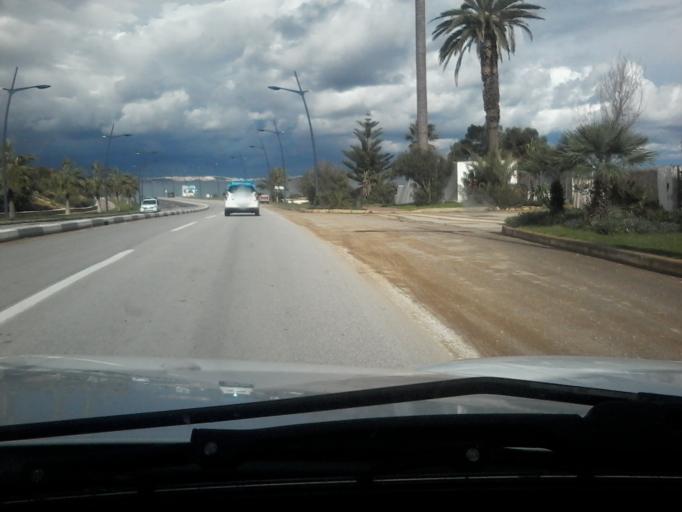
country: ES
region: Ceuta
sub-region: Ceuta
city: Ceuta
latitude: 35.7760
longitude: -5.3486
